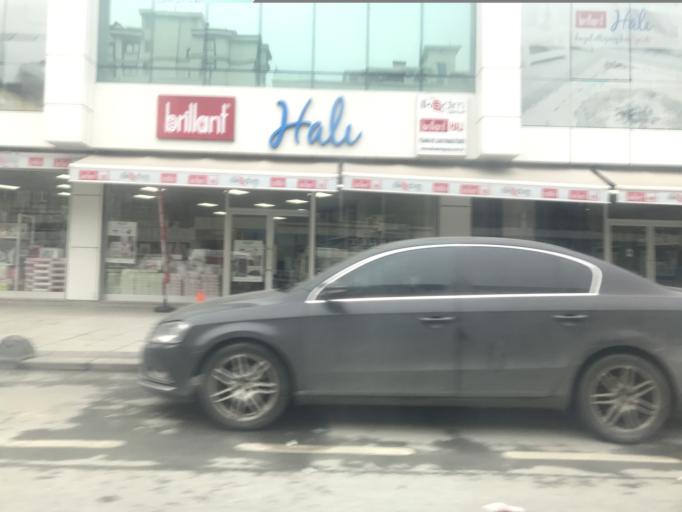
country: TR
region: Istanbul
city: Mahmutbey
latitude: 41.0368
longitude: 28.8342
